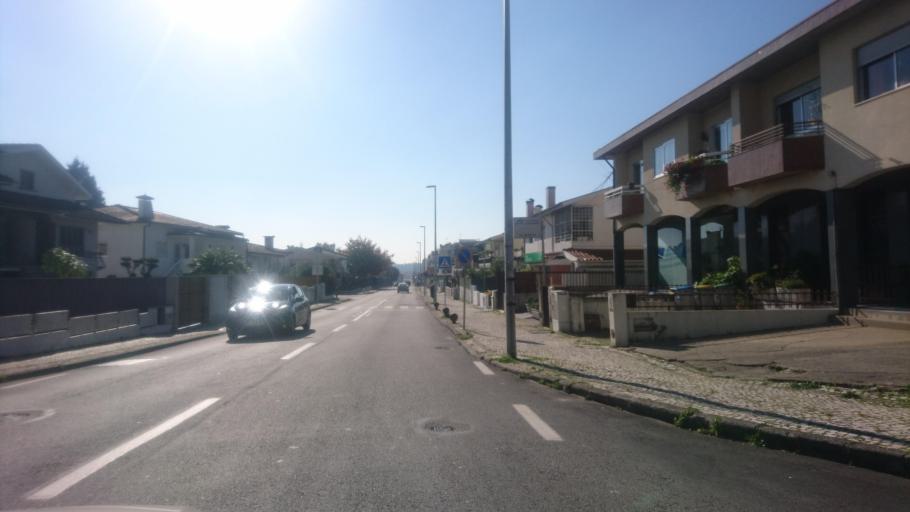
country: PT
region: Aveiro
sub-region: Santa Maria da Feira
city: Feira
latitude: 40.9260
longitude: -8.5583
